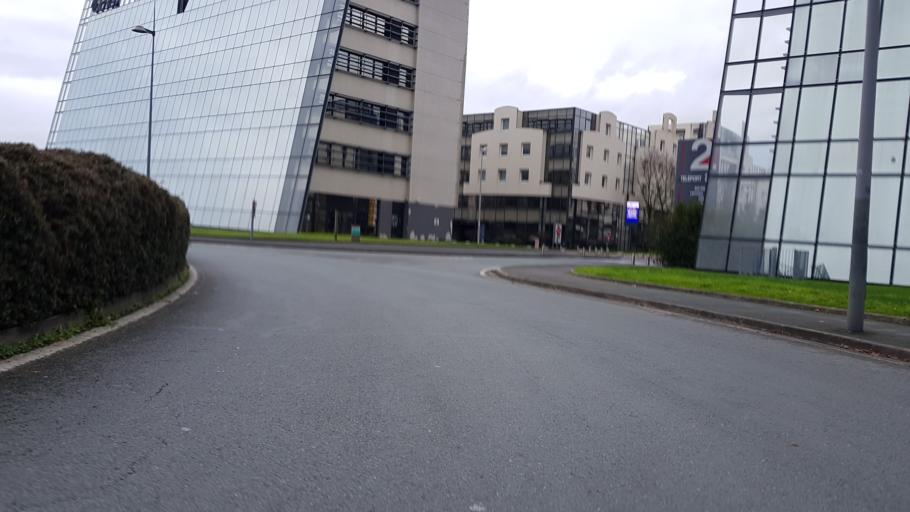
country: FR
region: Poitou-Charentes
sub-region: Departement de la Vienne
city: Chasseneuil-du-Poitou
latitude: 46.6631
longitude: 0.3609
